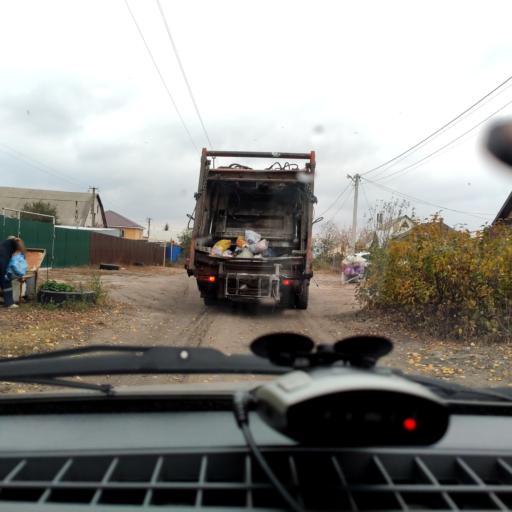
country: RU
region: Voronezj
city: Pridonskoy
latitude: 51.7019
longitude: 39.0714
